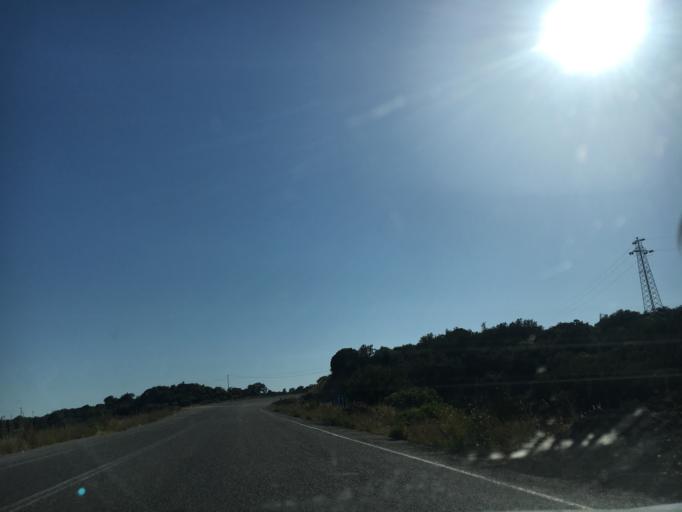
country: TR
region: Canakkale
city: Behram
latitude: 39.5059
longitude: 26.4040
